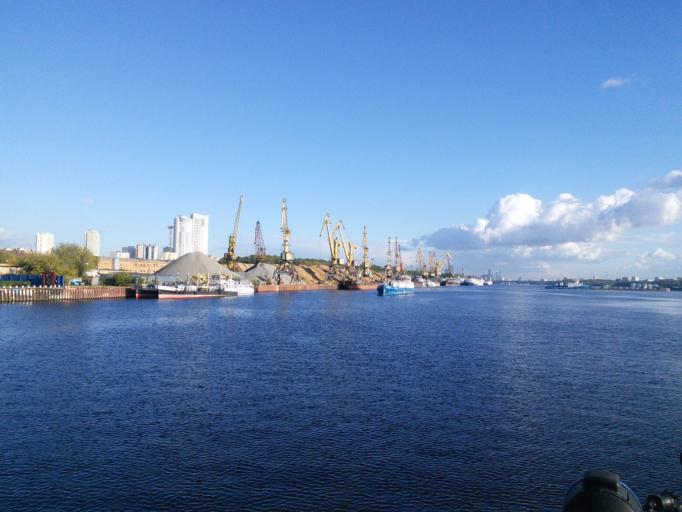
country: RU
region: Moskovskaya
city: Levoberezhnyy
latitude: 55.8663
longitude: 37.4551
